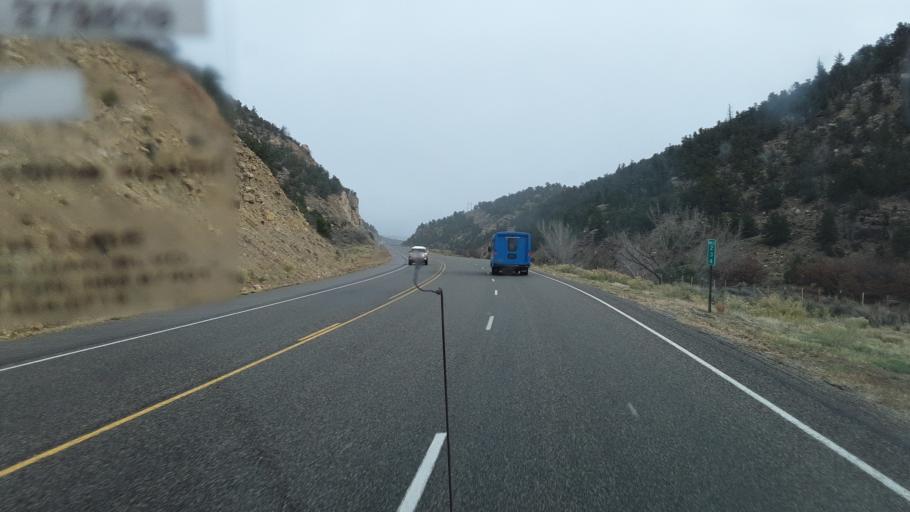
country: US
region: New Mexico
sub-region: Rio Arriba County
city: Tierra Amarilla
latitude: 36.4147
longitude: -106.4821
